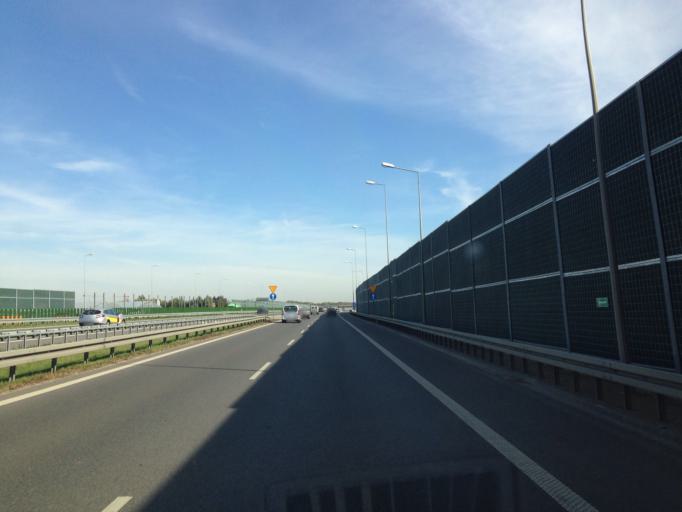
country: PL
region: Masovian Voivodeship
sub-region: Powiat warszawski zachodni
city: Ozarow Mazowiecki
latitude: 52.1895
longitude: 20.7853
